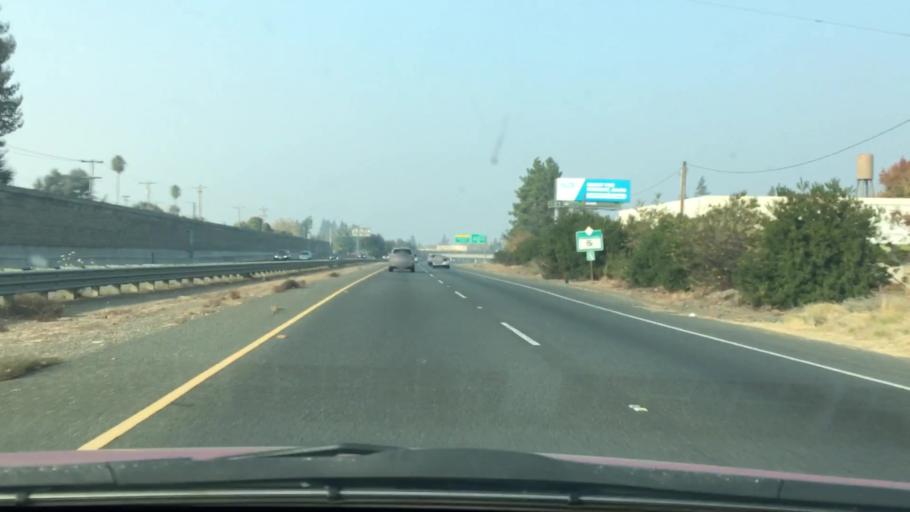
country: US
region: California
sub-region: Napa County
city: Napa
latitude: 38.3141
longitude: -122.3068
